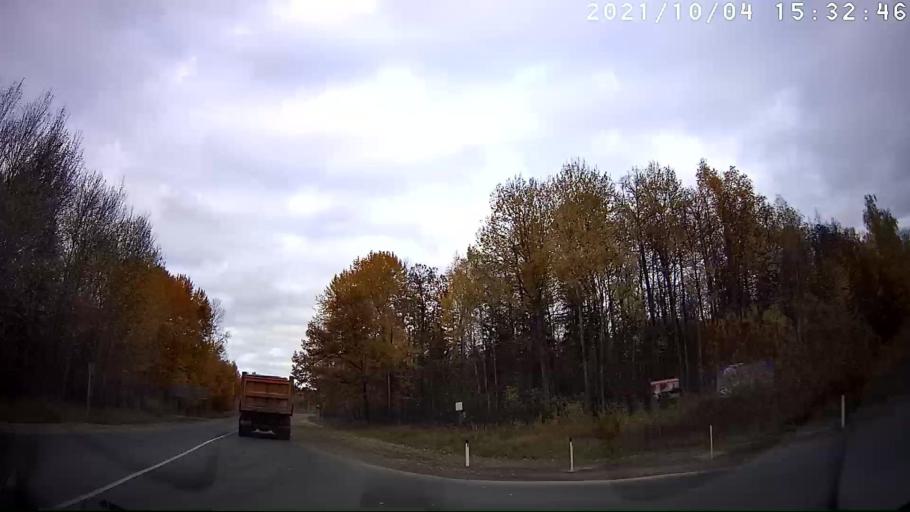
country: RU
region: Mariy-El
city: Yoshkar-Ola
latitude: 56.5675
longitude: 47.9742
